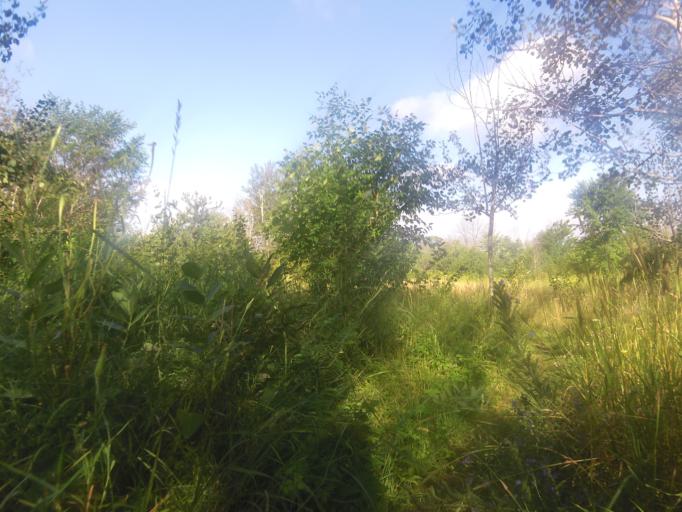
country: CA
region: Ontario
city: Bells Corners
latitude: 45.3288
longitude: -75.7973
